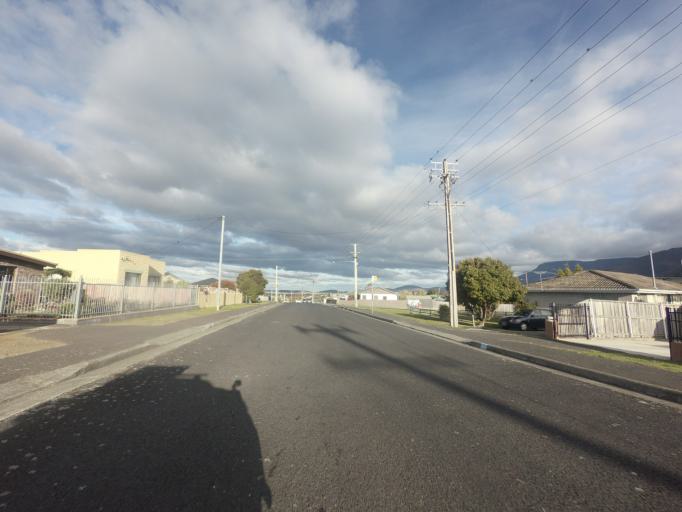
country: AU
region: Tasmania
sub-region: Glenorchy
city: Claremont
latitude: -42.7844
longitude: 147.2444
